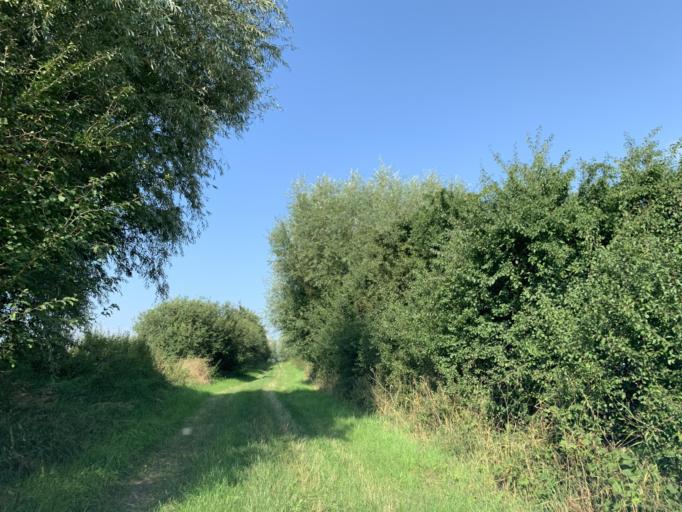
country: DE
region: Mecklenburg-Vorpommern
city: Blankensee
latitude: 53.3956
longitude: 13.2428
